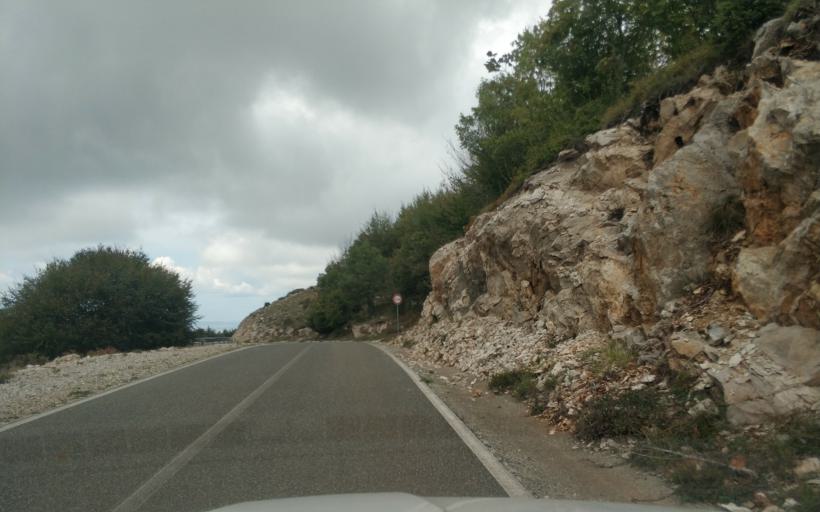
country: AL
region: Durres
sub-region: Rrethi i Krujes
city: Kruje
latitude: 41.5188
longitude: 19.8076
